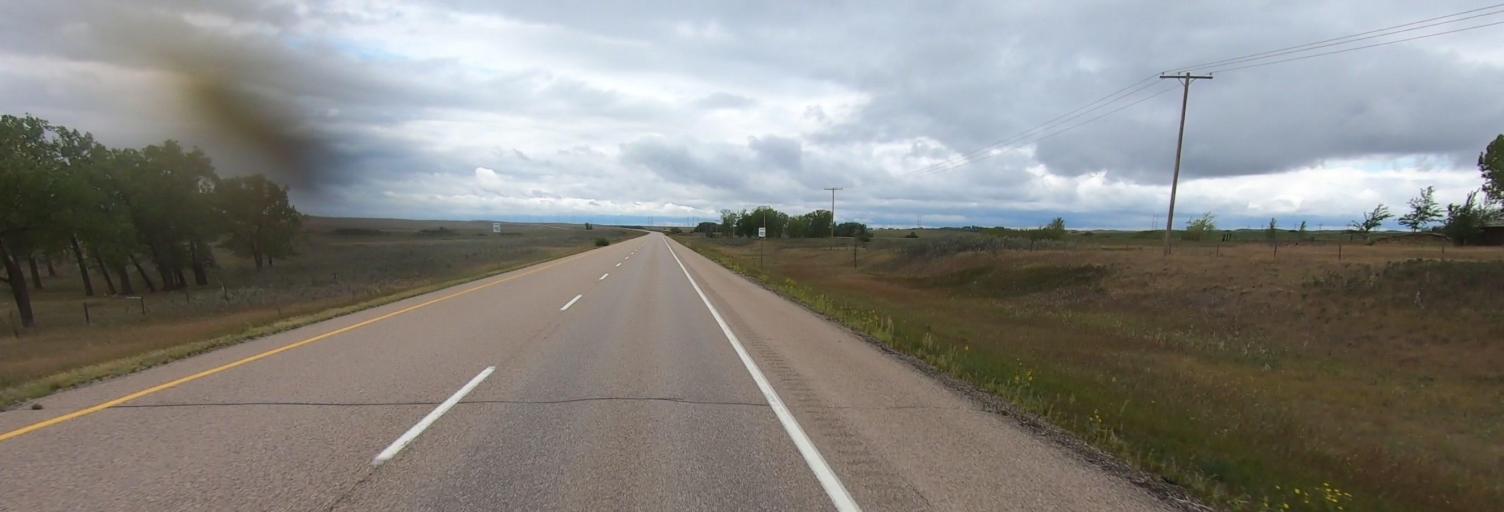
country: CA
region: Saskatchewan
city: Gravelbourg
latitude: 50.4739
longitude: -106.7684
